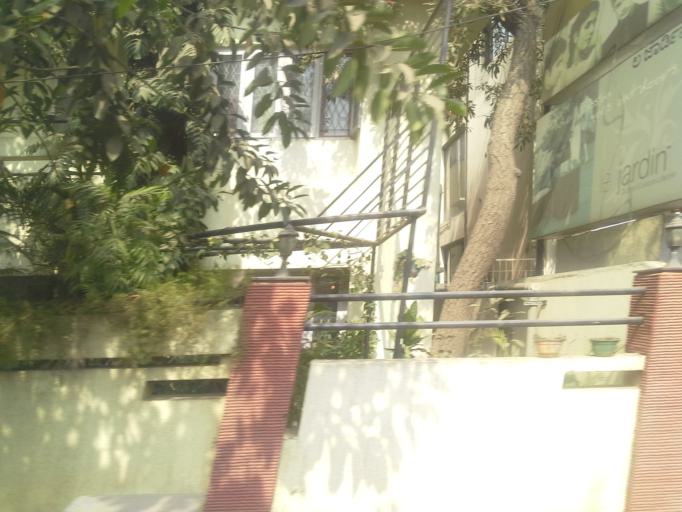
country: IN
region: Karnataka
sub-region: Bangalore Urban
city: Bangalore
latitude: 12.9758
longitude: 77.6166
